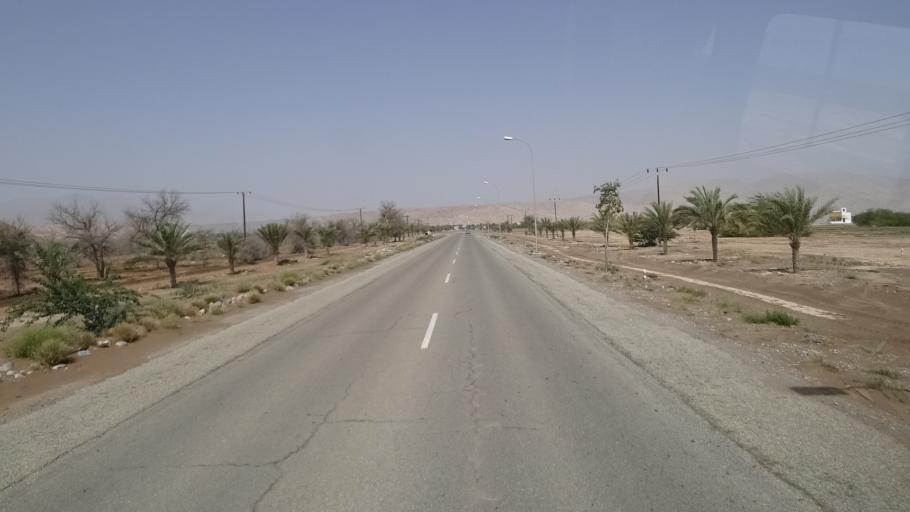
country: OM
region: Muhafazat Masqat
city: Muscat
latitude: 23.2163
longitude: 58.9290
